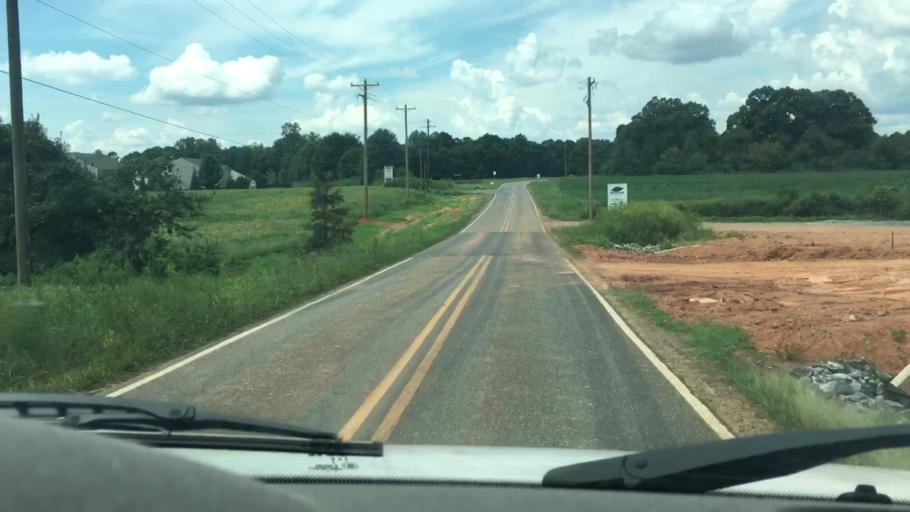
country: US
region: North Carolina
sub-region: Iredell County
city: Troutman
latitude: 35.6661
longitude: -80.8289
